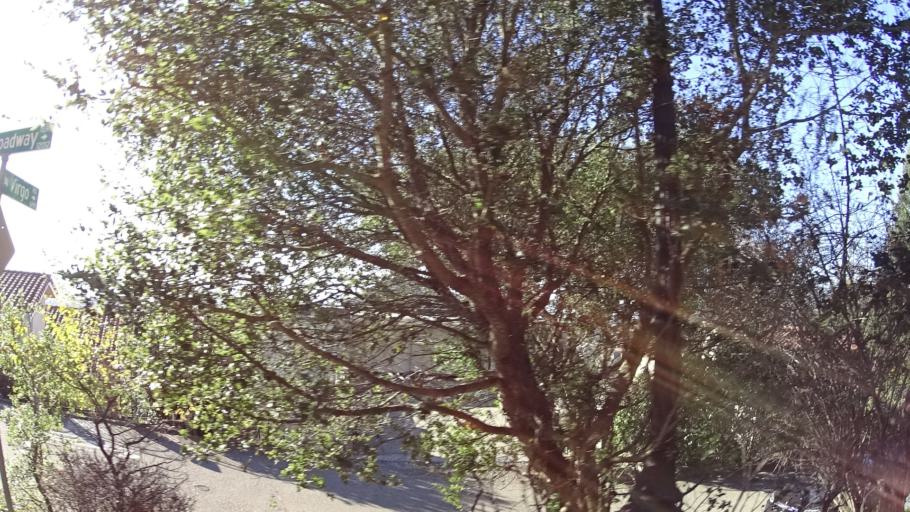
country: US
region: California
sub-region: Alameda County
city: Piedmont
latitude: 37.8414
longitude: -122.2153
